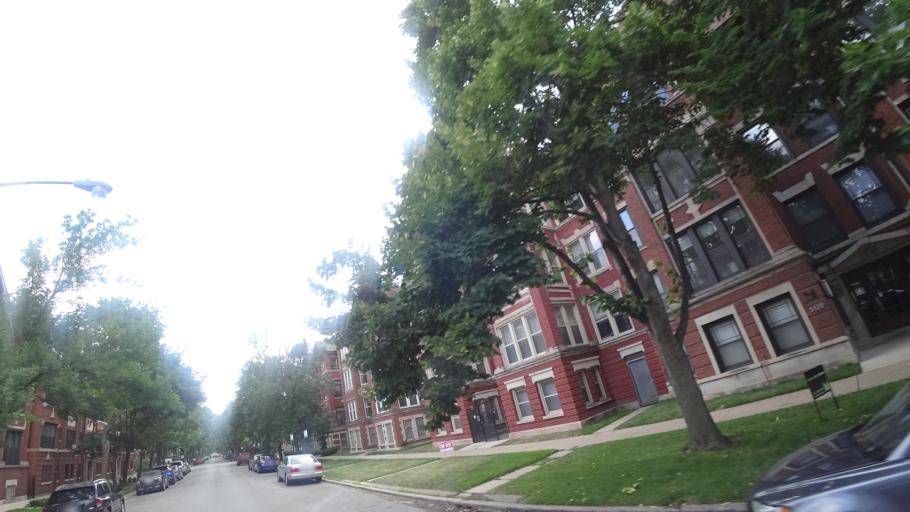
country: US
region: Illinois
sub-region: Cook County
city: Chicago
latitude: 41.8017
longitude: -87.5998
